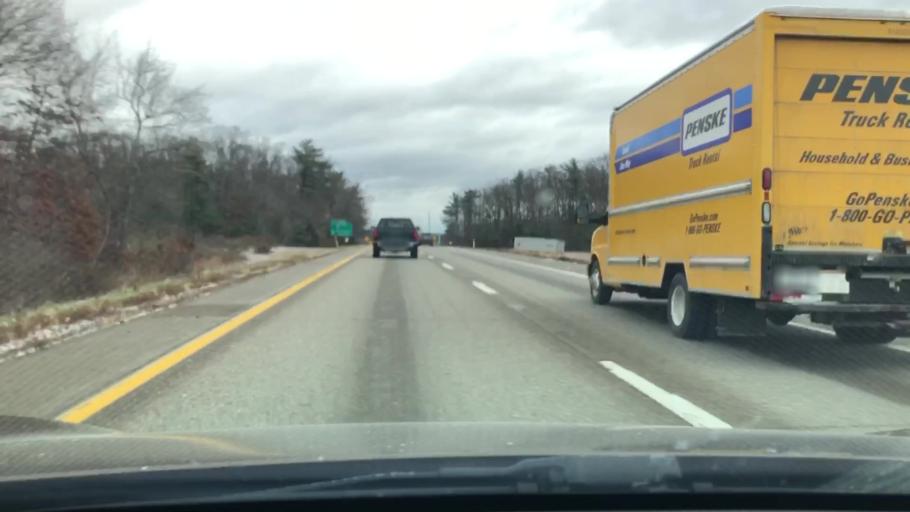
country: US
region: Pennsylvania
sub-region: Luzerne County
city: Conyngham
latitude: 41.0445
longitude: -76.0178
